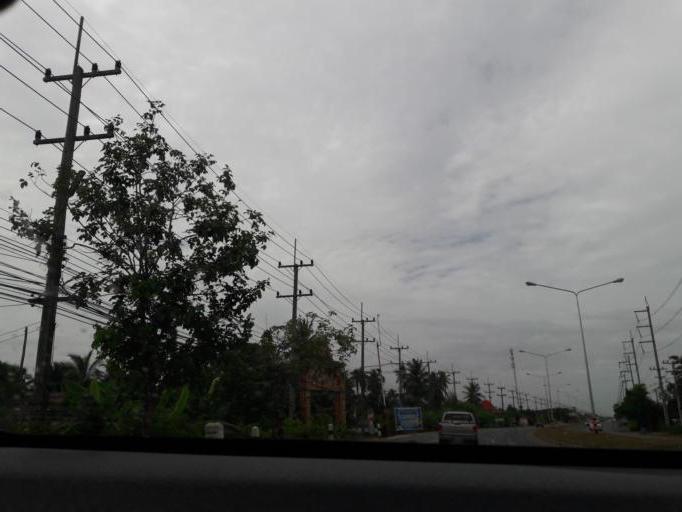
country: TH
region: Ratchaburi
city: Damnoen Saduak
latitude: 13.5735
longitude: 99.9708
